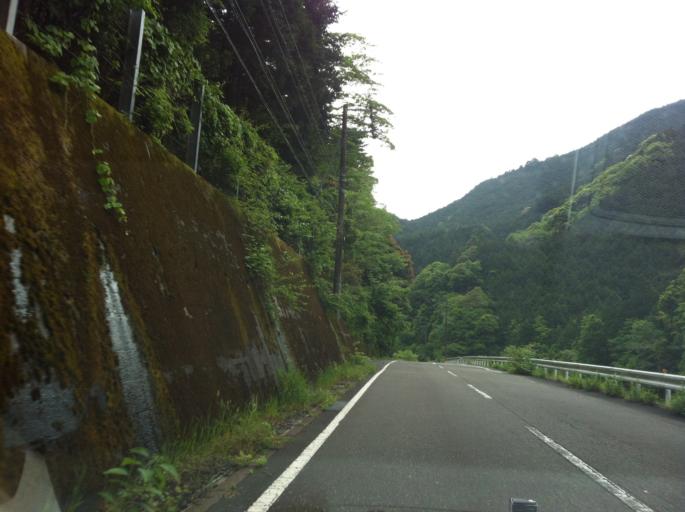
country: JP
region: Shizuoka
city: Shizuoka-shi
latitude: 35.1684
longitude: 138.3144
